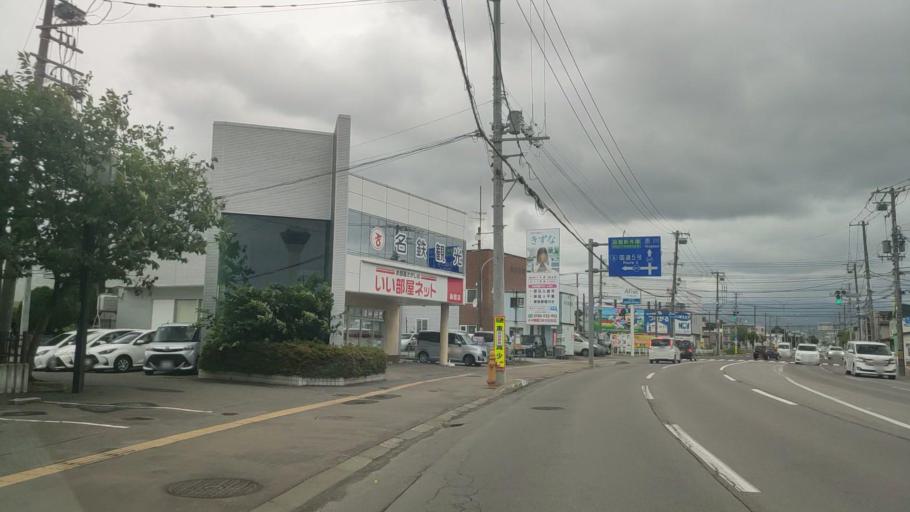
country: JP
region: Hokkaido
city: Hakodate
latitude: 41.7993
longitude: 140.7501
